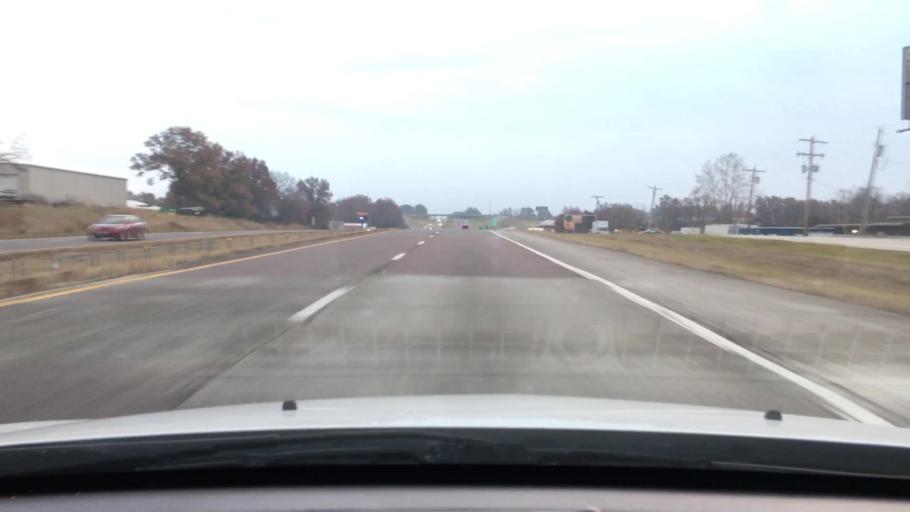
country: US
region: Missouri
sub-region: Boone County
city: Hallsville
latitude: 38.9538
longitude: -92.1388
